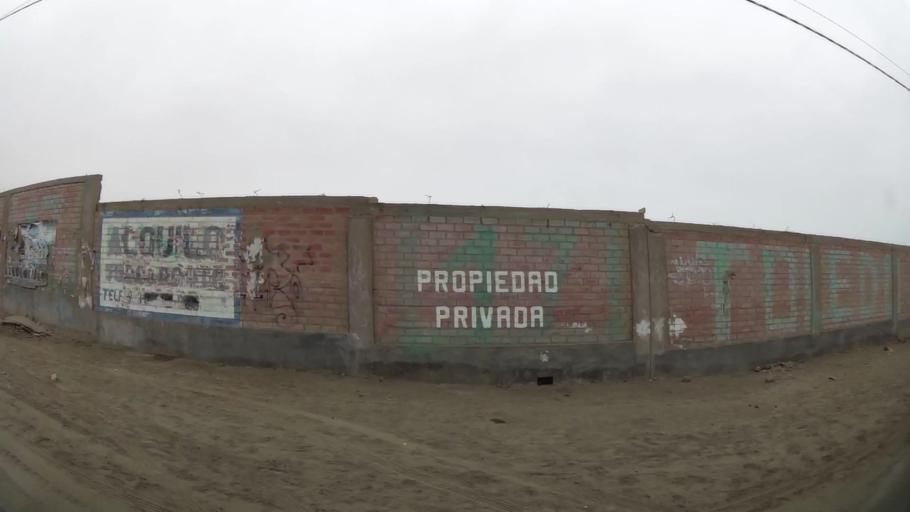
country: PE
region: Lima
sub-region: Lima
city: Punta Hermosa
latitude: -12.3184
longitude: -76.8316
